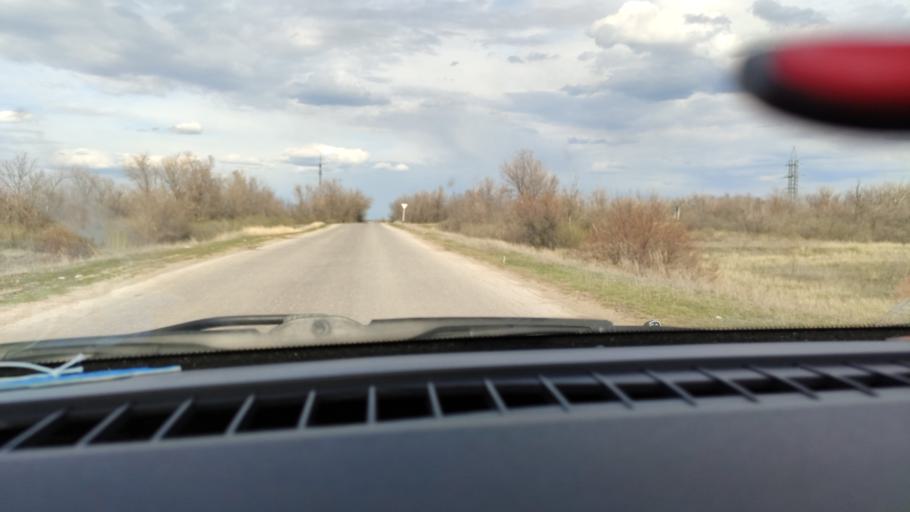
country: RU
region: Saratov
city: Rovnoye
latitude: 50.9423
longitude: 46.1275
